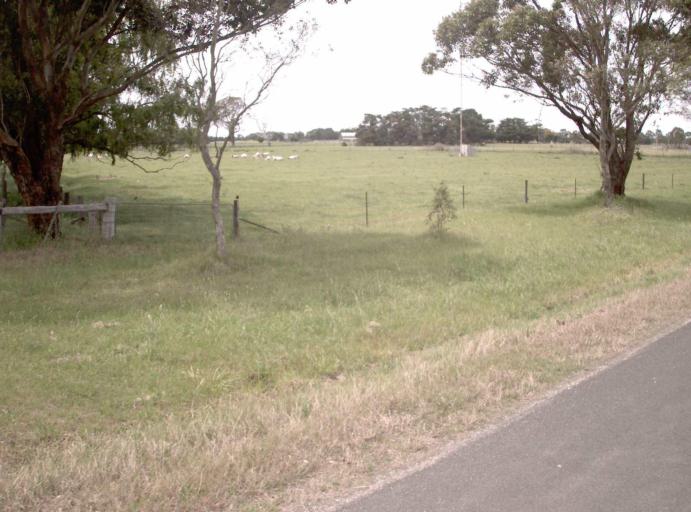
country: AU
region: Victoria
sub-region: Wellington
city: Sale
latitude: -38.0582
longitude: 147.0269
